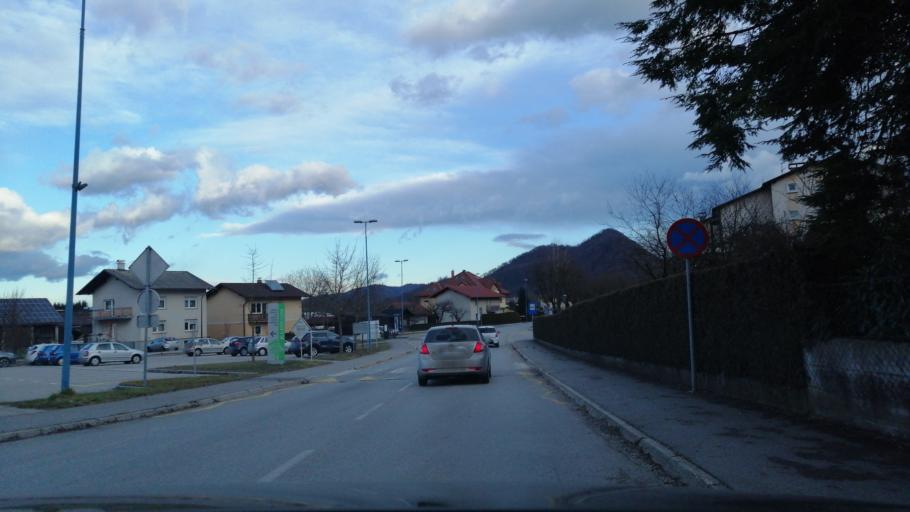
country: SI
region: Medvode
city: Medvode
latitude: 46.1347
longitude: 14.4106
